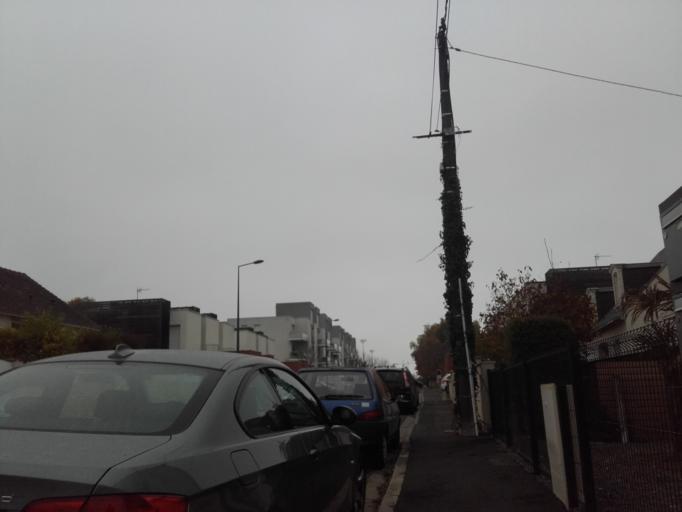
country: FR
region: Centre
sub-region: Departement d'Indre-et-Loire
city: Tours
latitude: 47.4132
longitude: 0.7115
